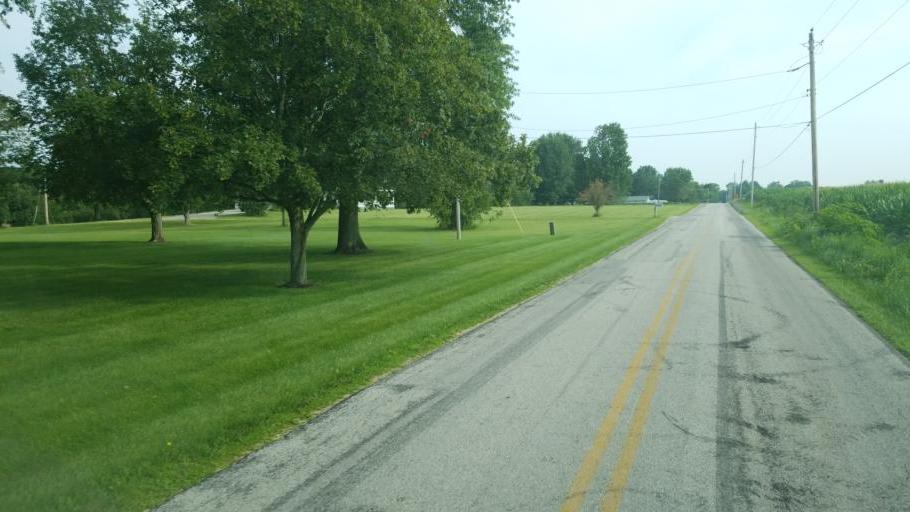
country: US
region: Ohio
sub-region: Marion County
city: Marion
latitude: 40.4913
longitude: -83.0537
